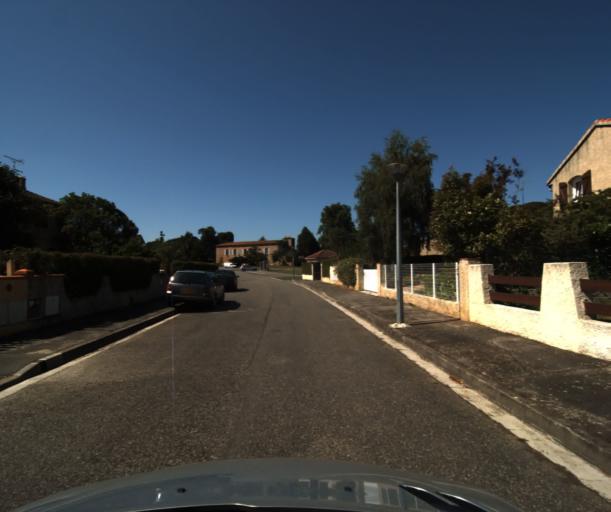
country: FR
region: Midi-Pyrenees
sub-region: Departement de la Haute-Garonne
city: Roquettes
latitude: 43.5008
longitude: 1.3655
